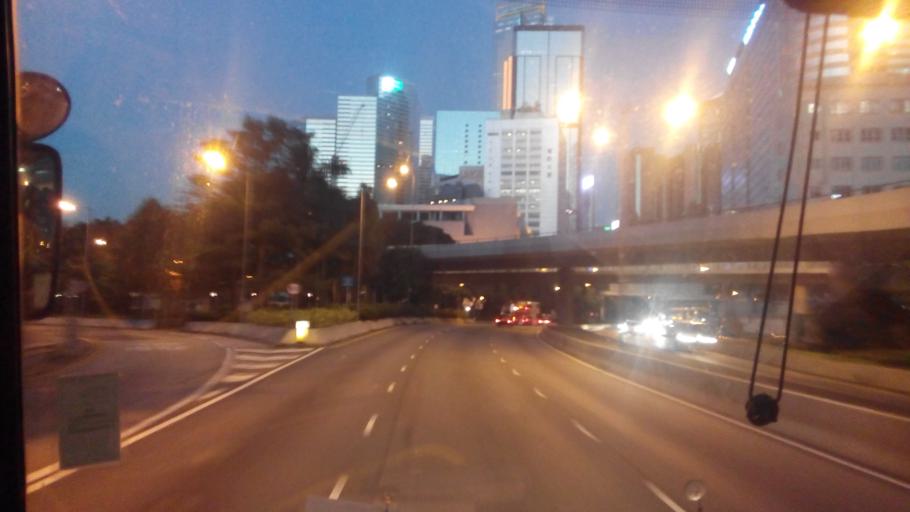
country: HK
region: Wanchai
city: Wan Chai
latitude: 22.2795
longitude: 114.1673
